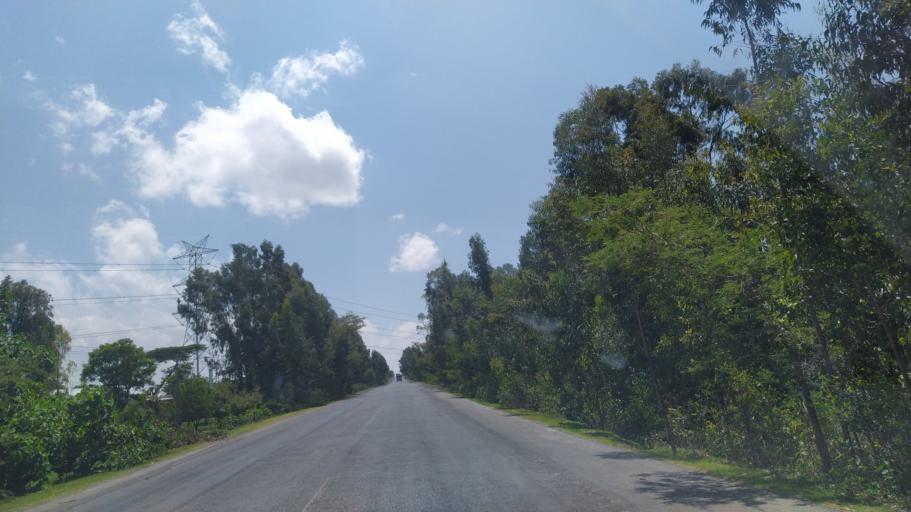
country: ET
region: Southern Nations, Nationalities, and People's Region
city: Butajira
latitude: 7.7529
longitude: 38.1291
